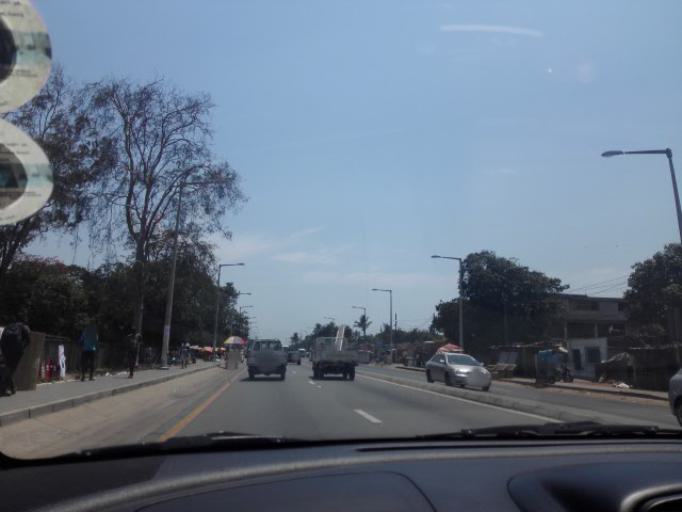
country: MZ
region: Maputo City
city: Maputo
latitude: -25.9253
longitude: 32.5588
